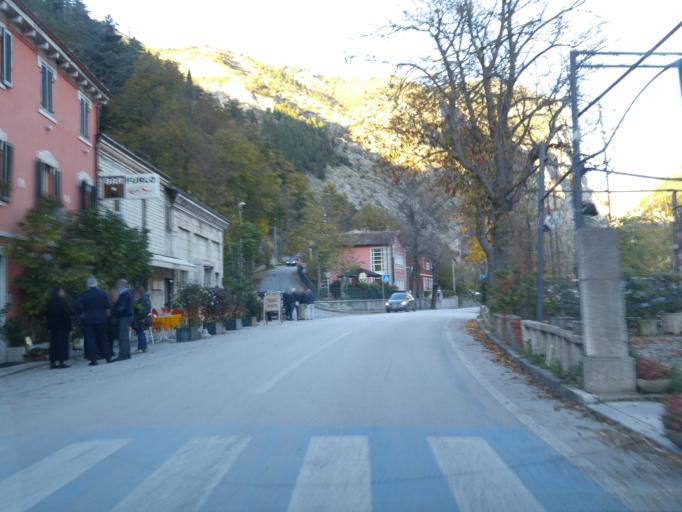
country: IT
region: The Marches
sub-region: Provincia di Pesaro e Urbino
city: Acqualagna
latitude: 43.6382
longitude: 12.7134
